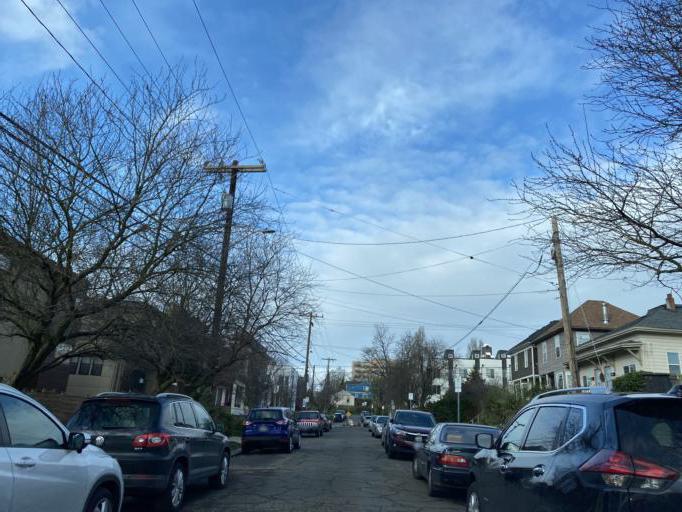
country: US
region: Washington
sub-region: King County
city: Seattle
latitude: 47.6028
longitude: -122.3113
